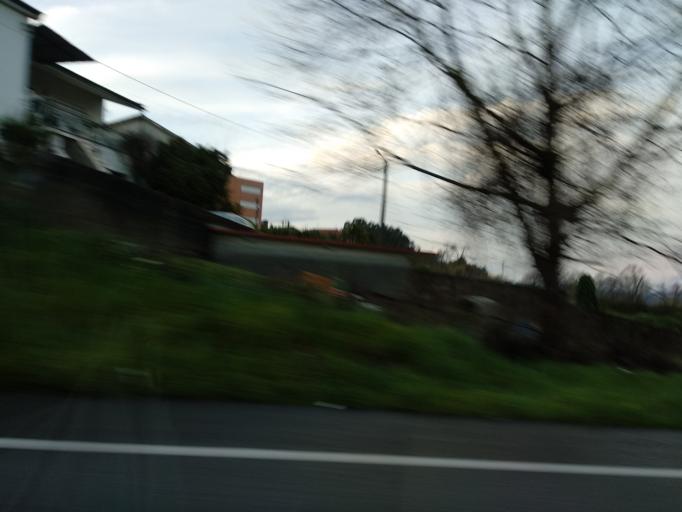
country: PT
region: Braga
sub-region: Braga
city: Oliveira
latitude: 41.5078
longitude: -8.4610
